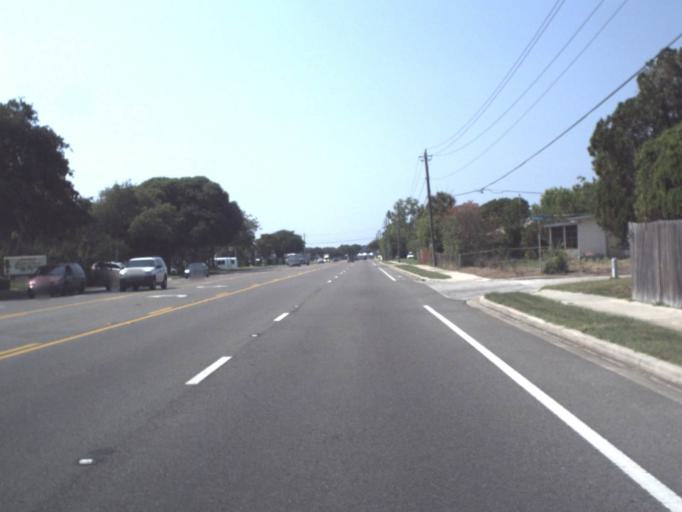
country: US
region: Florida
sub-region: Saint Johns County
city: Saint Augustine Beach
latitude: 29.8683
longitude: -81.2834
